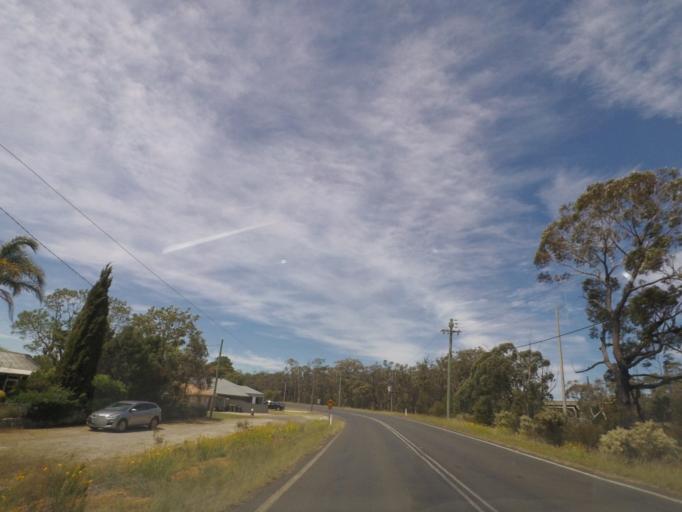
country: AU
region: New South Wales
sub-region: Wollondilly
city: Buxton
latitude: -34.3239
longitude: 150.5713
